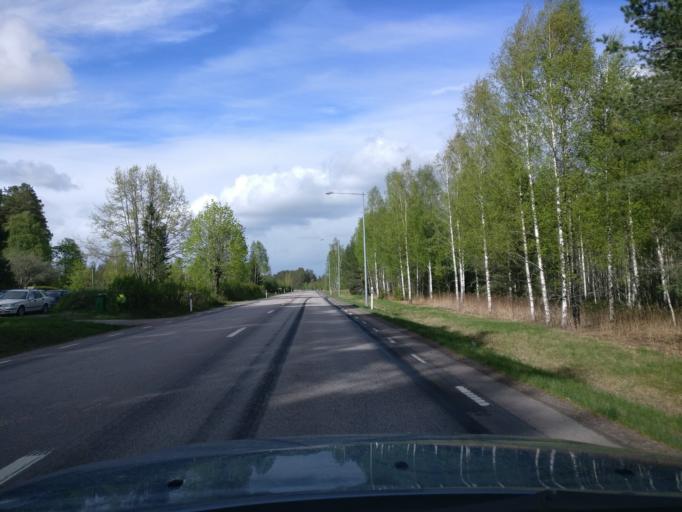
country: SE
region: Vaermland
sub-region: Forshaga Kommun
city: Forshaga
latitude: 59.4944
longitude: 13.4282
